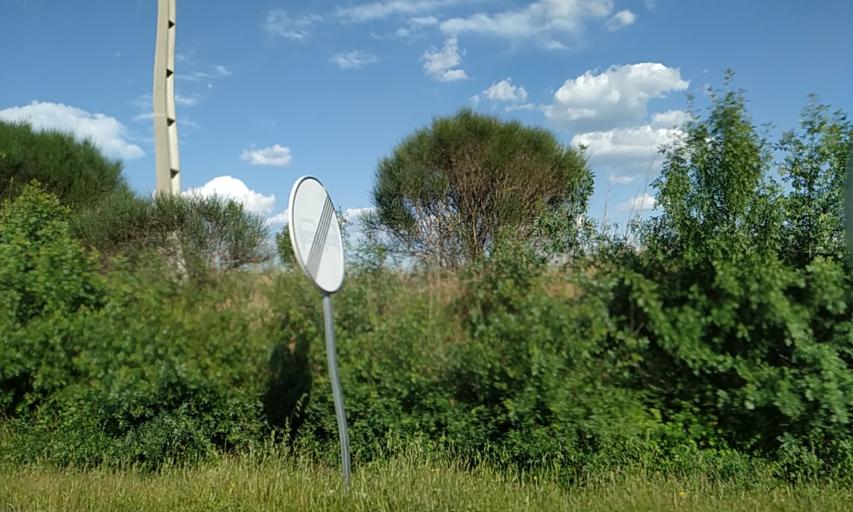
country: PT
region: Evora
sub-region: Estremoz
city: Estremoz
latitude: 38.9701
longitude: -7.4922
